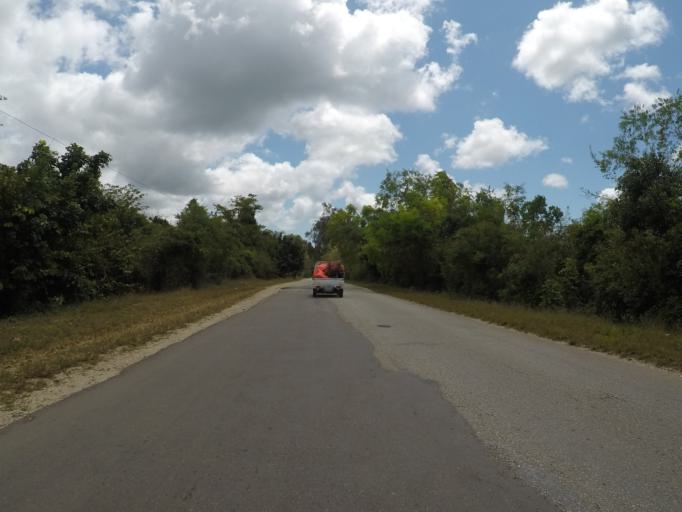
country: TZ
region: Zanzibar Central/South
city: Mahonda
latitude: -6.2824
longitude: 39.4155
